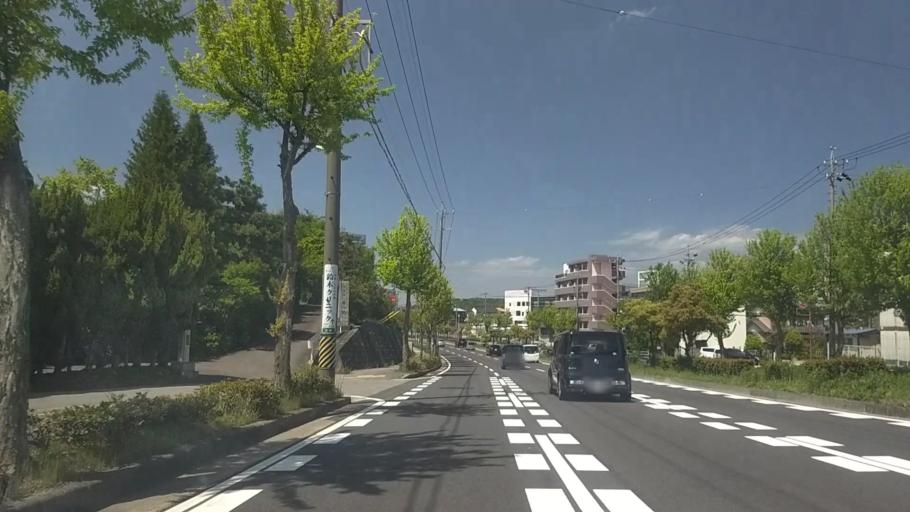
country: JP
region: Aichi
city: Okazaki
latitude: 34.9560
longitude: 137.1897
